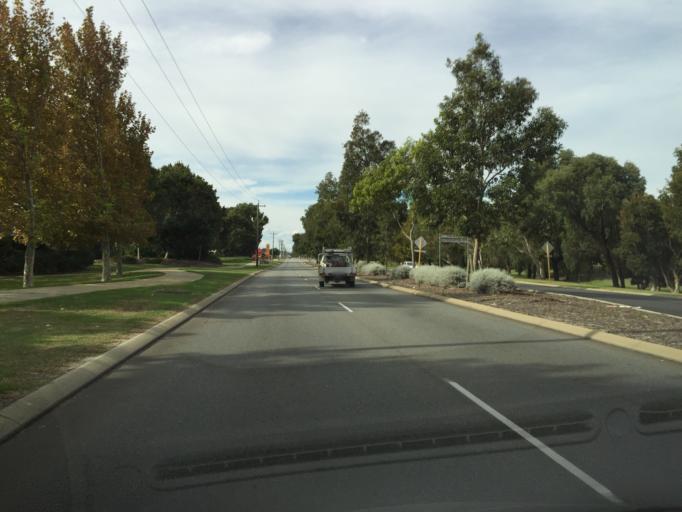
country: AU
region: Western Australia
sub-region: Canning
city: Willetton
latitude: -32.0689
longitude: 115.8966
